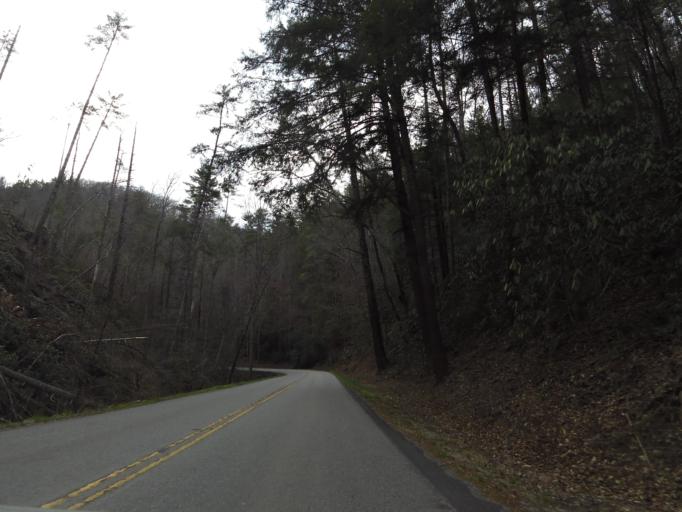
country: US
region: Tennessee
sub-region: Blount County
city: Wildwood
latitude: 35.6365
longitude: -83.7240
